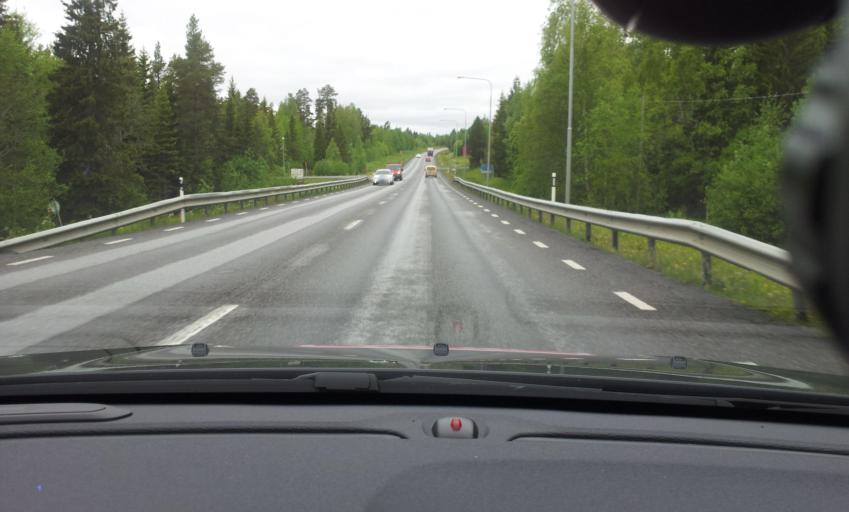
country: SE
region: Jaemtland
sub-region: Krokoms Kommun
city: Valla
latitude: 63.3064
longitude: 13.8305
